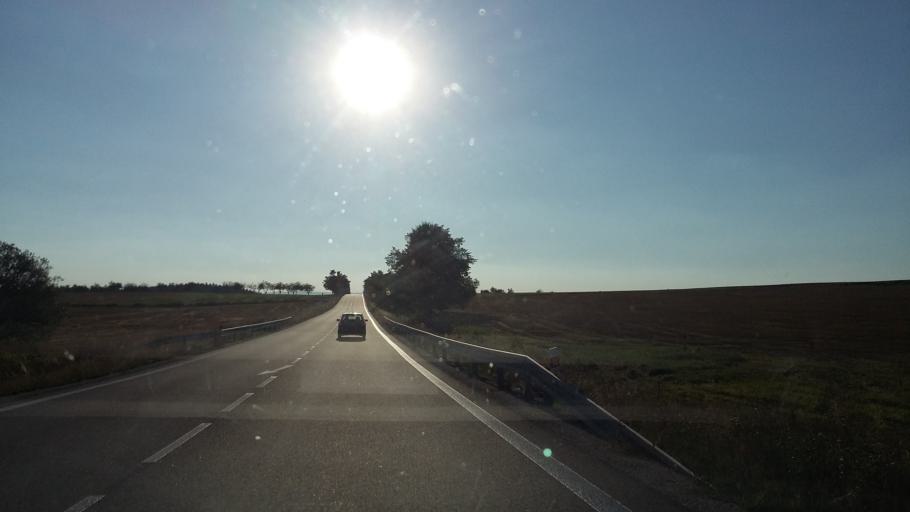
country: CZ
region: Vysocina
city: Kamenice
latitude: 49.3973
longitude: 15.7750
